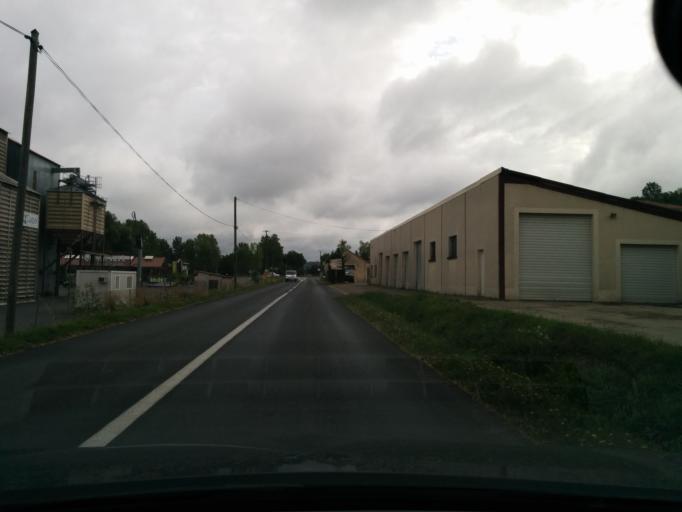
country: FR
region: Midi-Pyrenees
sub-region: Departement du Lot
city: Montcuq
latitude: 44.3428
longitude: 1.2074
